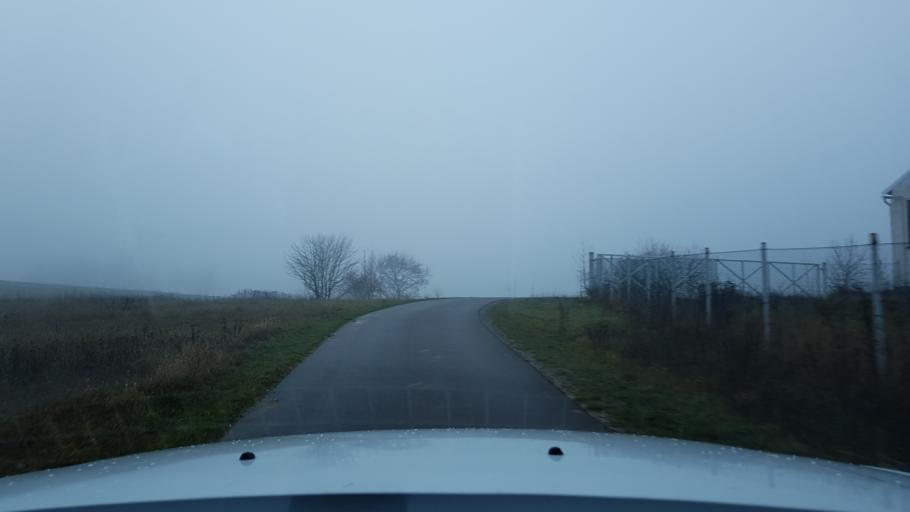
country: DE
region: Brandenburg
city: Mescherin
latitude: 53.2709
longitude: 14.4307
